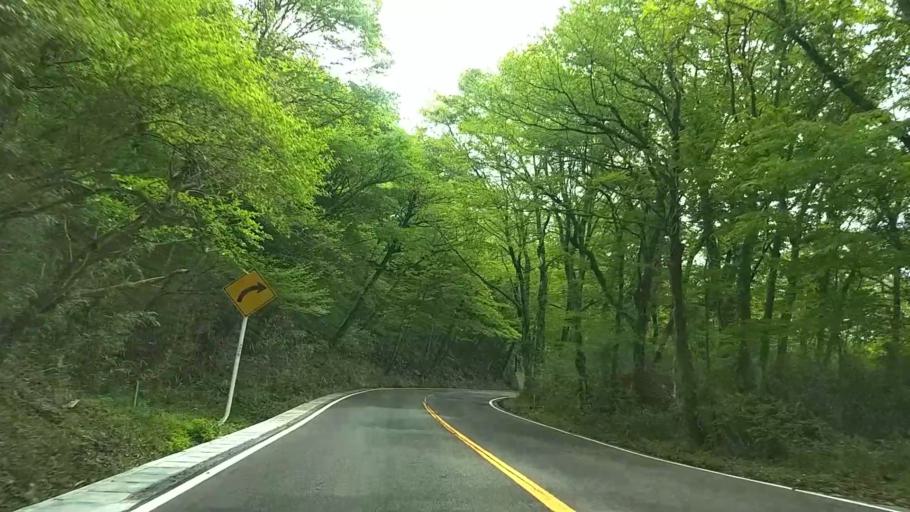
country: JP
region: Kanagawa
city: Hakone
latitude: 35.2314
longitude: 138.9986
